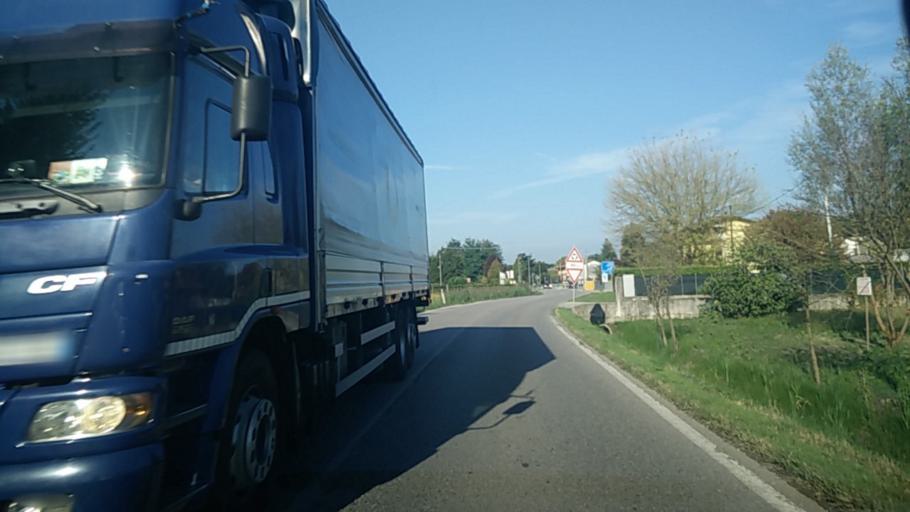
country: IT
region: Veneto
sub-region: Provincia di Padova
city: Torreselle
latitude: 45.6066
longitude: 12.0233
